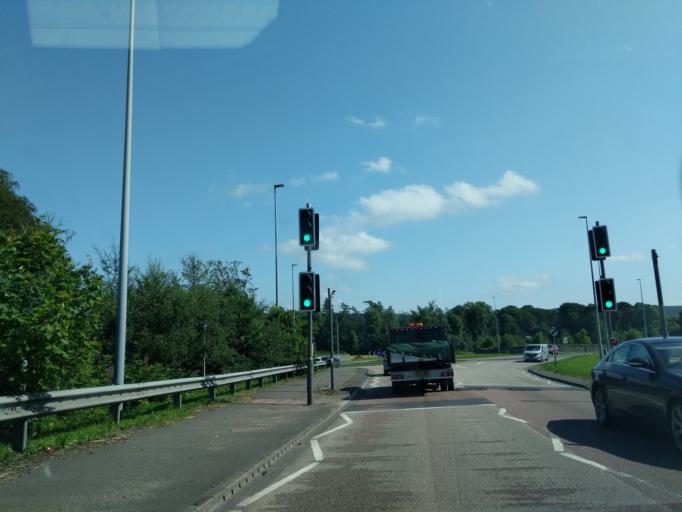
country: GB
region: Scotland
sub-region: Moray
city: Fochabers
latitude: 57.6197
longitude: -3.1048
